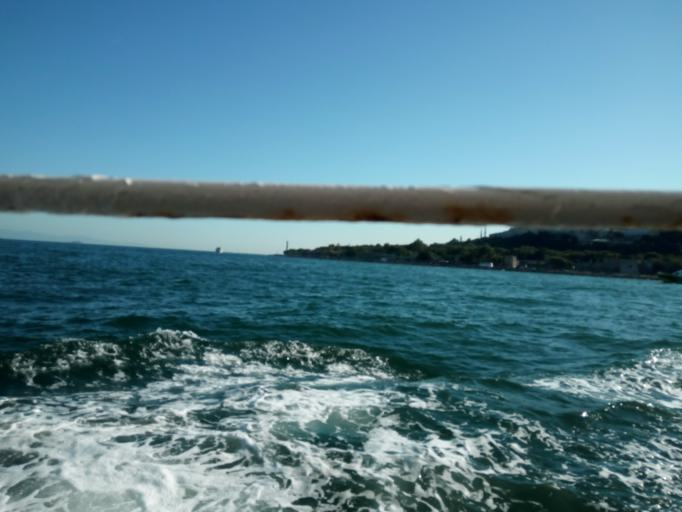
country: TR
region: Istanbul
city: Eminoenue
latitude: 41.0166
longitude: 28.9923
